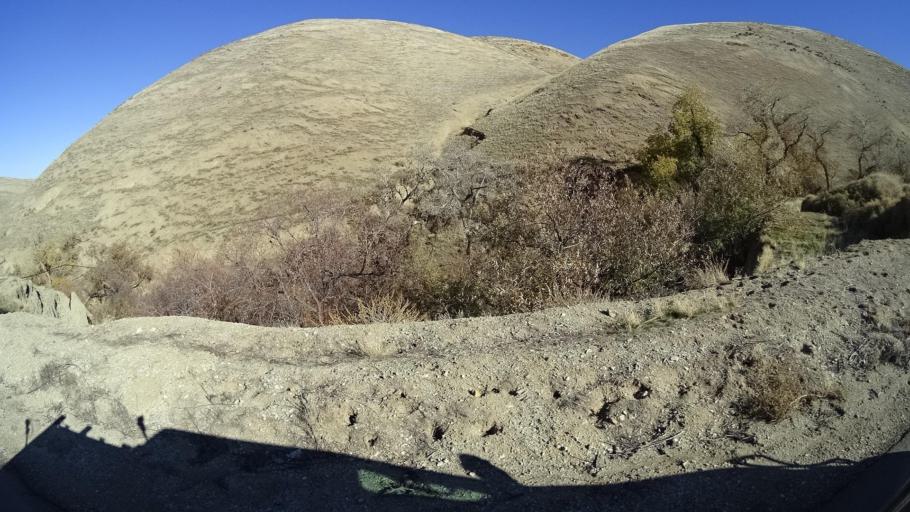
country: US
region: California
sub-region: Kern County
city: Maricopa
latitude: 34.9680
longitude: -119.4139
